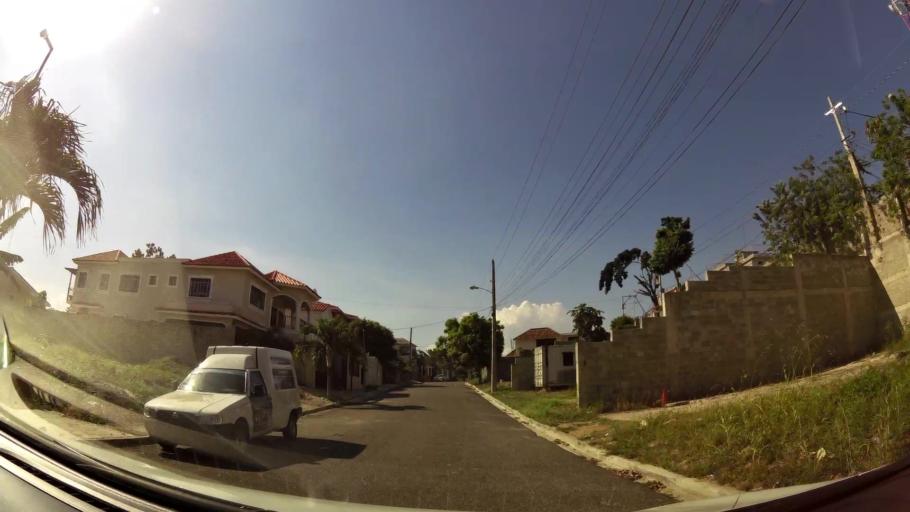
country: DO
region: Nacional
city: Bella Vista
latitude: 18.4610
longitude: -69.9826
